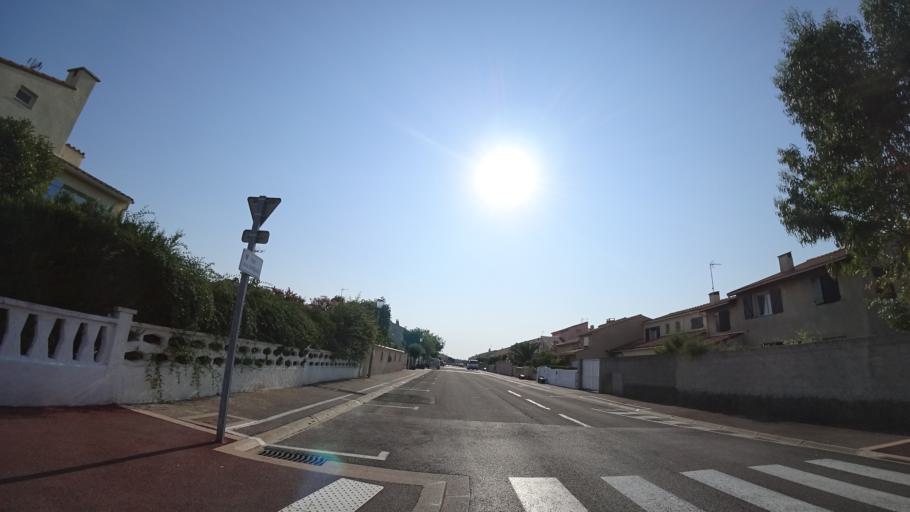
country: FR
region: Languedoc-Roussillon
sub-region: Departement des Pyrenees-Orientales
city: Bompas
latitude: 42.7257
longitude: 2.9365
